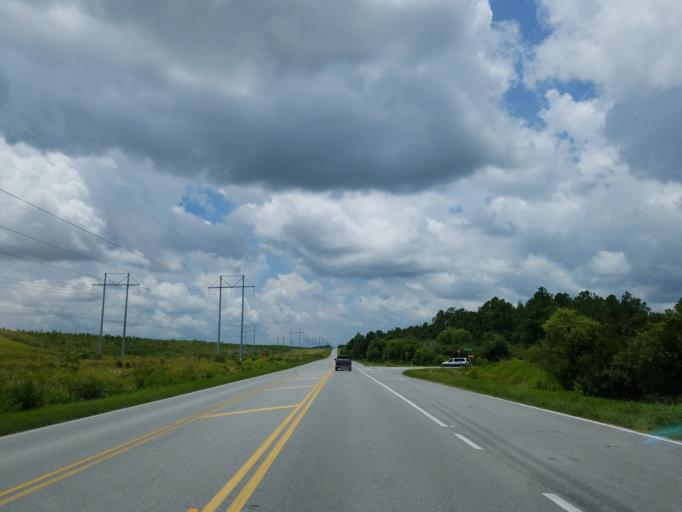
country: US
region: Florida
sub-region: Polk County
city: Fuller Heights
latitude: 27.8508
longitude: -82.0168
